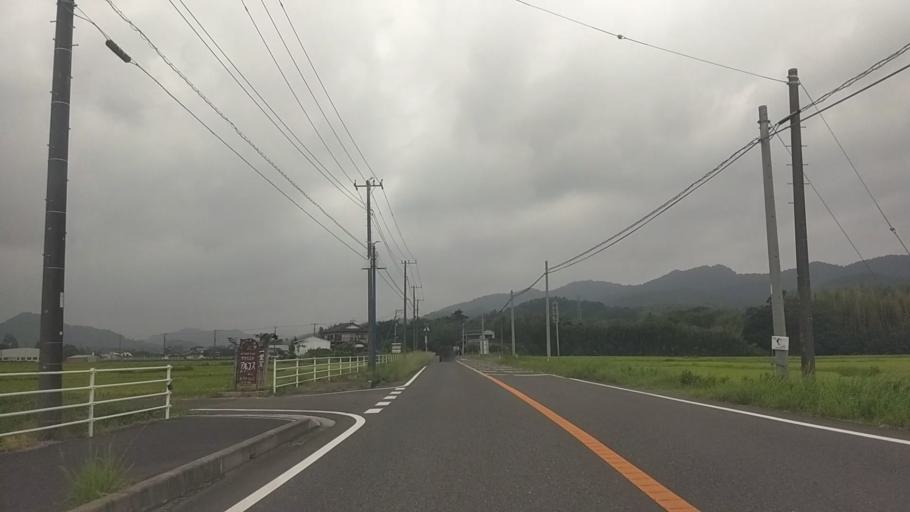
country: JP
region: Chiba
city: Kawaguchi
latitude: 35.1362
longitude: 139.9979
